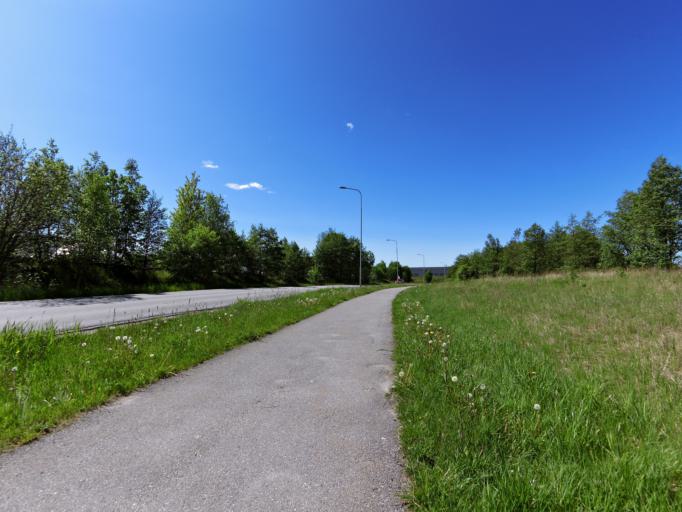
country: NO
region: Ostfold
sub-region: Fredrikstad
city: Fredrikstad
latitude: 59.2397
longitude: 10.9887
